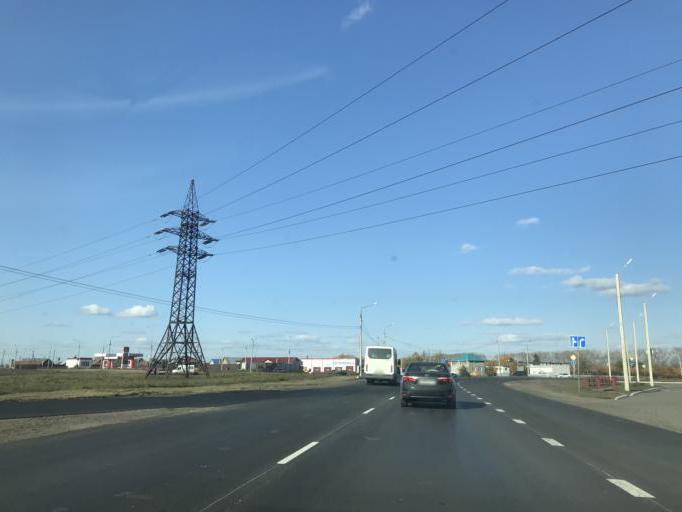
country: RU
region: Chelyabinsk
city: Roshchino
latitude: 55.2295
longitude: 61.2872
